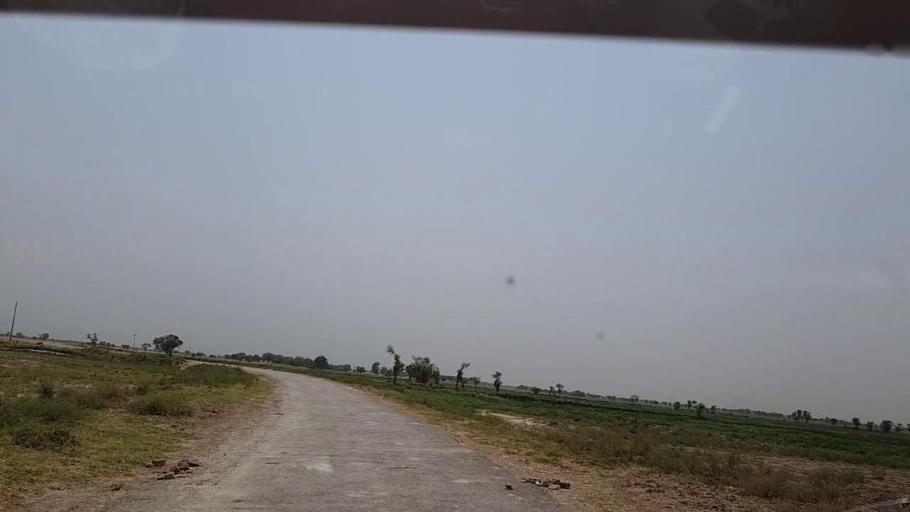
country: PK
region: Sindh
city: Khairpur Nathan Shah
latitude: 27.0166
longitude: 67.6569
